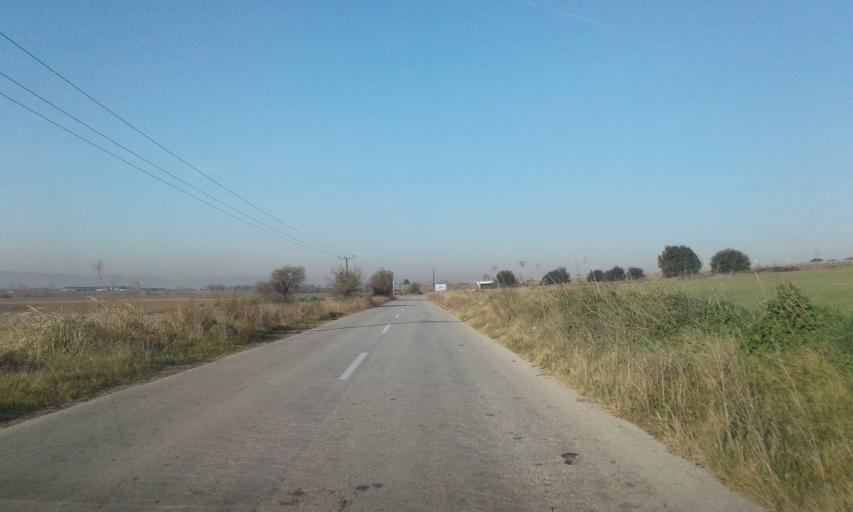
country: GR
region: Central Macedonia
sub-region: Nomos Thessalonikis
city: Kolchikon
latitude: 40.7071
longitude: 23.1879
